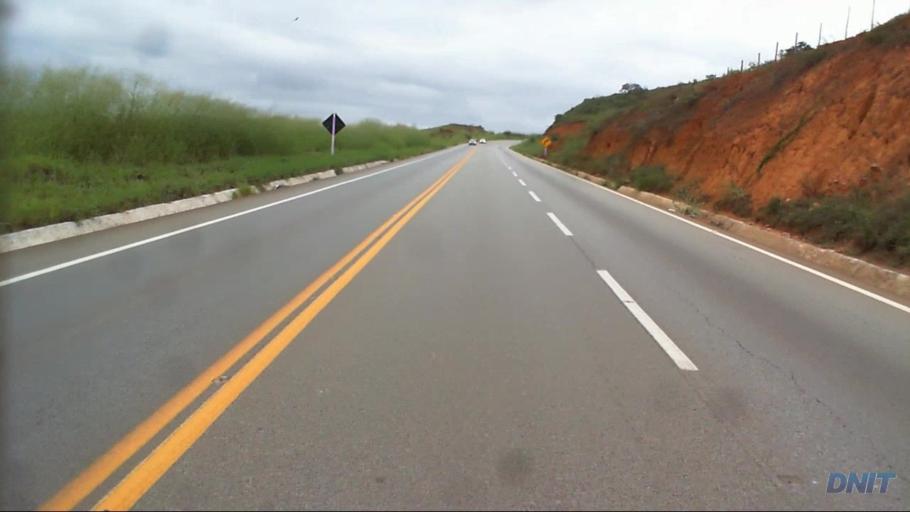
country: BR
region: Minas Gerais
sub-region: Nova Era
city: Nova Era
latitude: -19.7989
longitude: -43.0551
